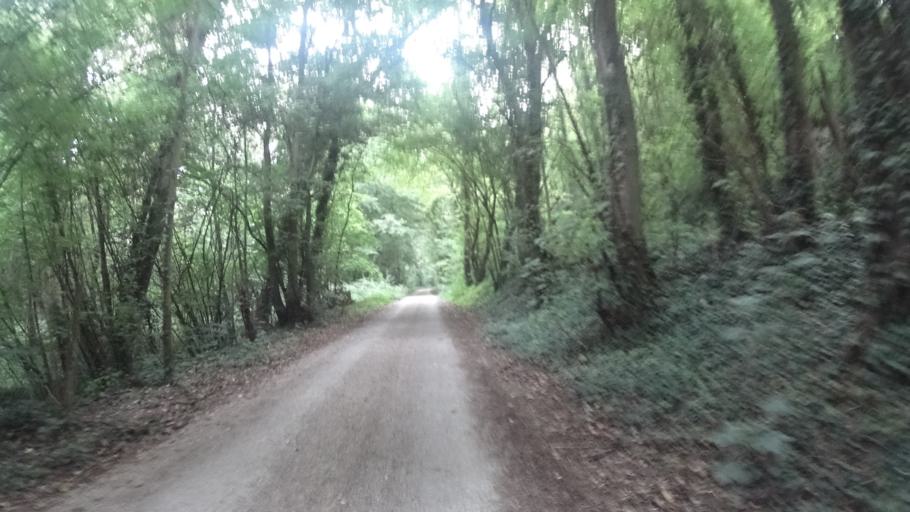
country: FR
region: Picardie
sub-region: Departement de l'Aisne
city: Origny-Sainte-Benoite
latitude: 49.8562
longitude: 3.5015
